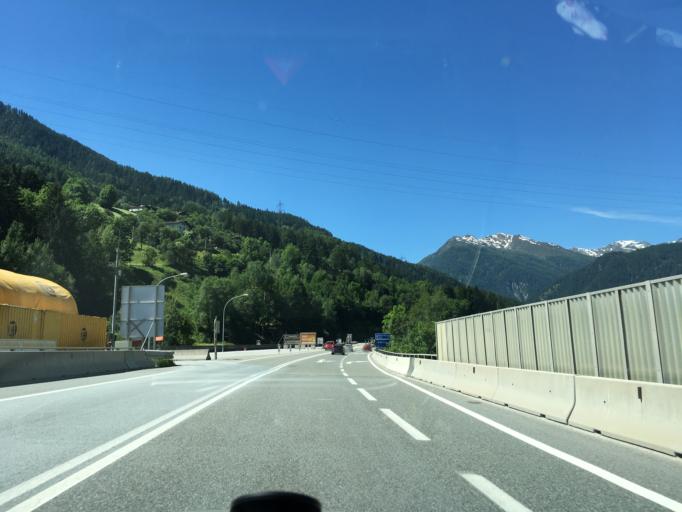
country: AT
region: Tyrol
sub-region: Politischer Bezirk Landeck
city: Stanz bei Landeck
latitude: 47.1407
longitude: 10.5412
